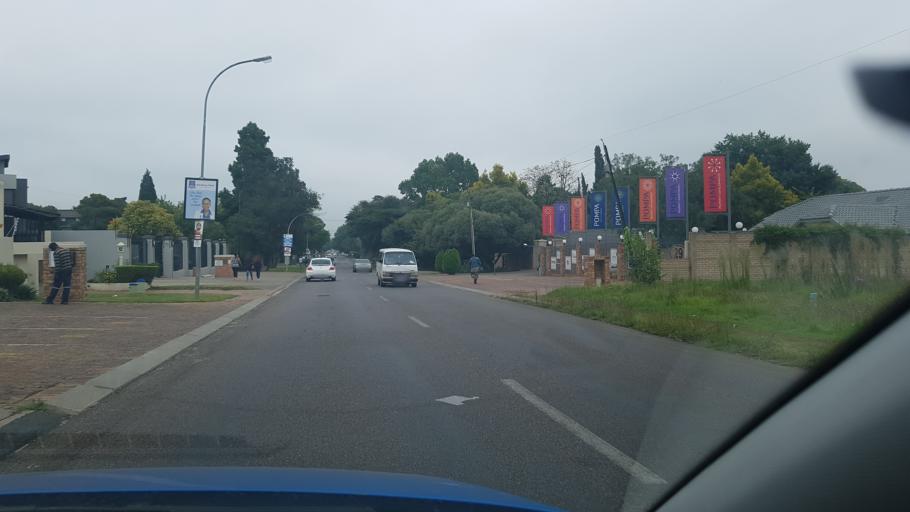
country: ZA
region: Gauteng
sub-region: Ekurhuleni Metropolitan Municipality
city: Germiston
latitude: -26.1681
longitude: 28.1550
